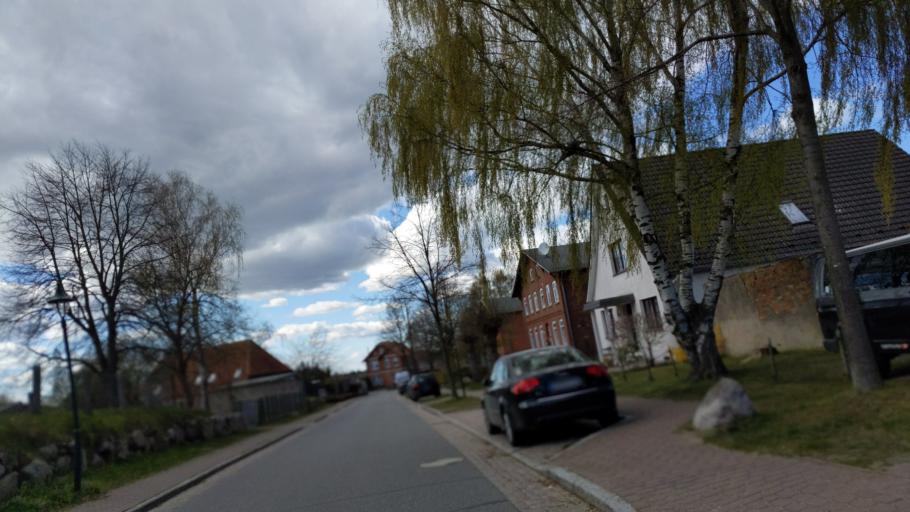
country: DE
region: Mecklenburg-Vorpommern
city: Selmsdorf
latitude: 53.8799
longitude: 10.8625
